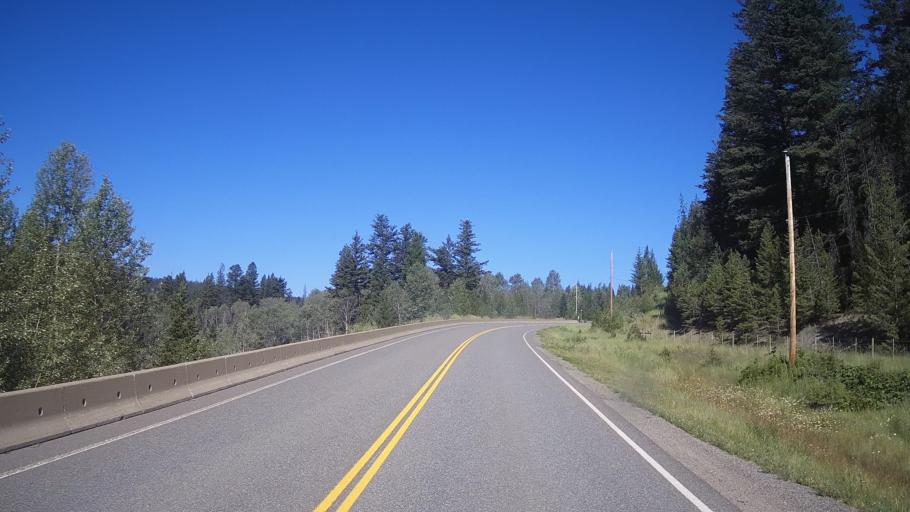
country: CA
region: British Columbia
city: Kamloops
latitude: 51.4766
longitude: -120.5588
